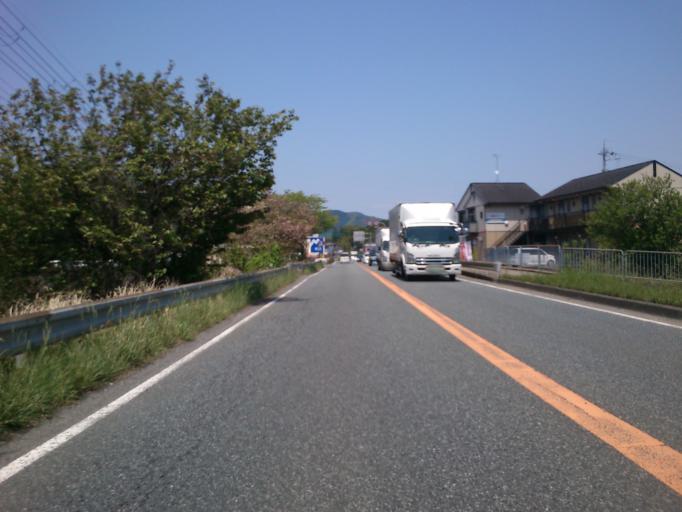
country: JP
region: Kyoto
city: Fukuchiyama
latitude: 35.3070
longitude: 135.1034
